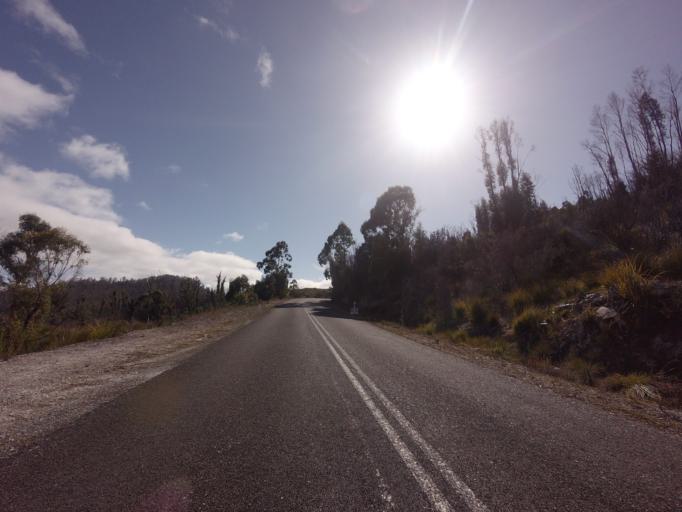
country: AU
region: Tasmania
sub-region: Huon Valley
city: Geeveston
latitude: -42.8475
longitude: 146.2390
